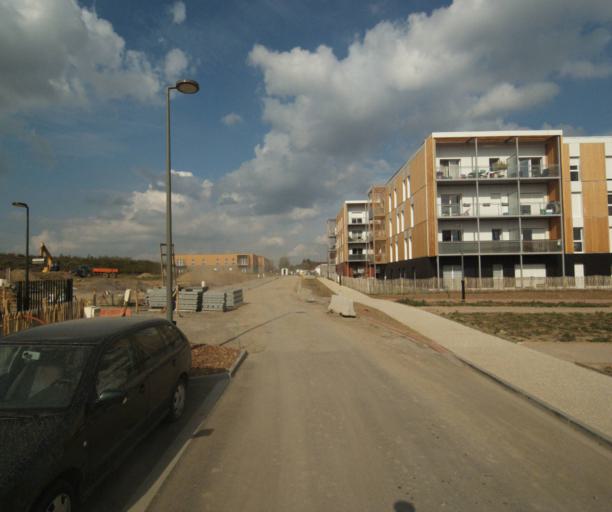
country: FR
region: Nord-Pas-de-Calais
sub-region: Departement du Nord
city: Hallennes-lez-Haubourdin
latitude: 50.6158
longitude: 2.9564
